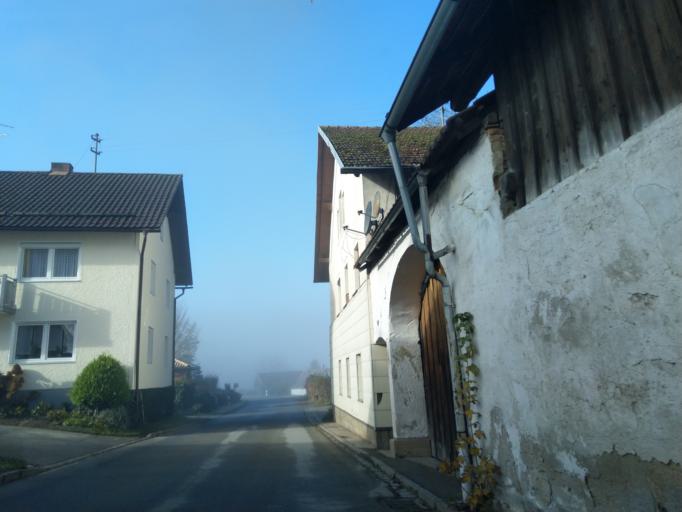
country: DE
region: Bavaria
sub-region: Lower Bavaria
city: Aussernzell
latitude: 48.7616
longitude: 13.2295
